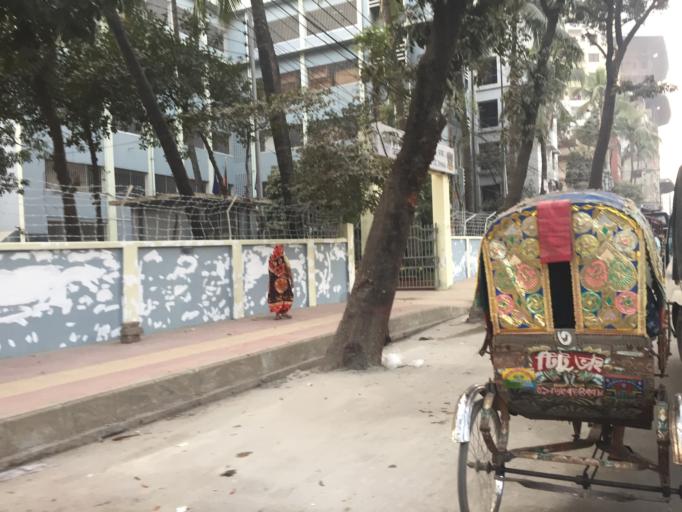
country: BD
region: Dhaka
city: Paltan
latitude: 23.7381
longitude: 90.4172
